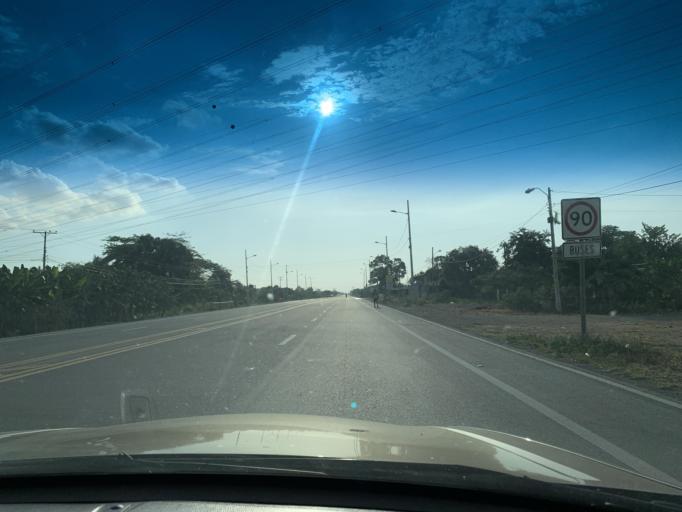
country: EC
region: Guayas
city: Naranjito
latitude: -2.2576
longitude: -79.5719
